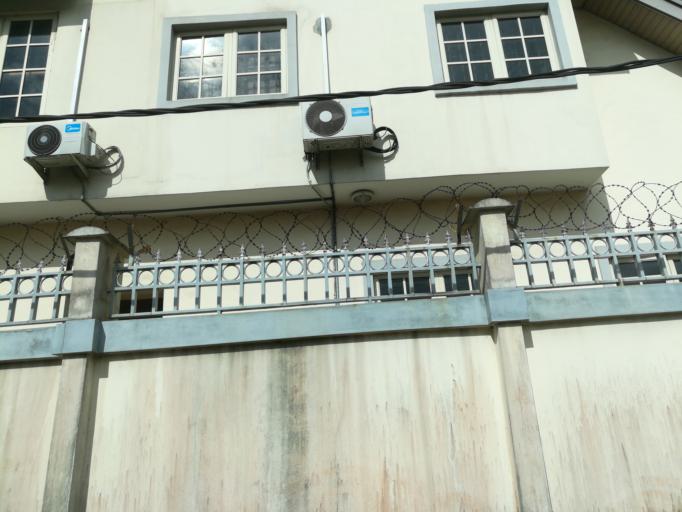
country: NG
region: Lagos
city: Ojota
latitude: 6.5754
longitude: 3.3641
